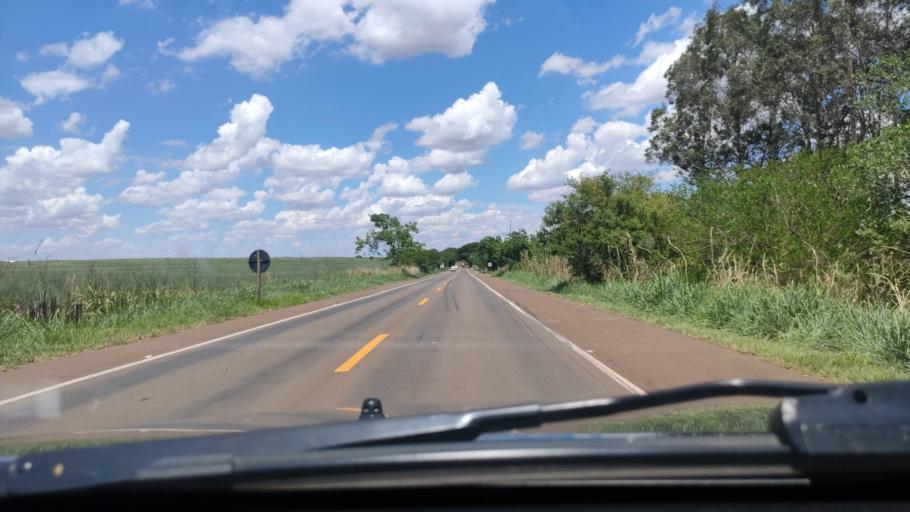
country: BR
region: Sao Paulo
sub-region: Boa Esperanca Do Sul
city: Boa Esperanca do Sul
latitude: -22.0698
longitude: -48.4240
